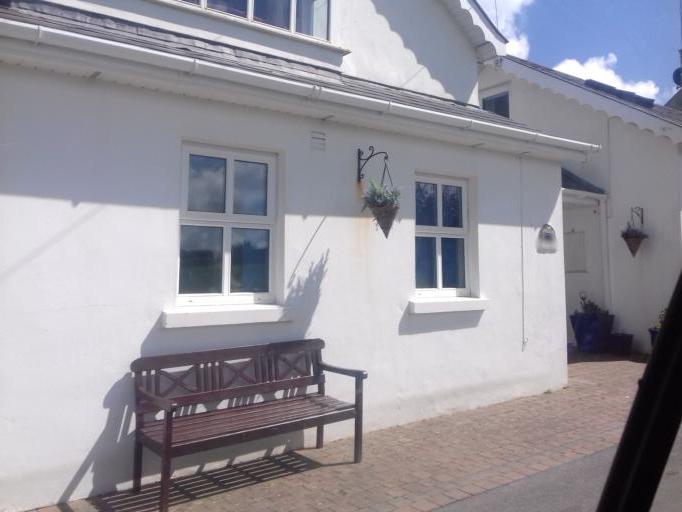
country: IE
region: Munster
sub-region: Waterford
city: Dunmore East
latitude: 52.2218
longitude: -6.9351
